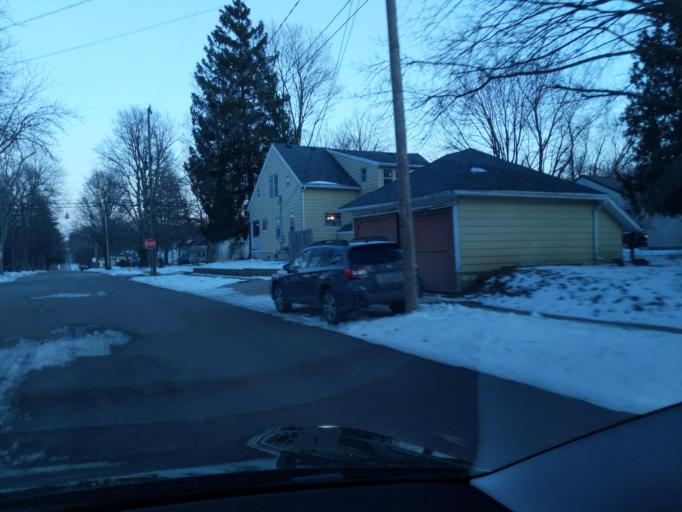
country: US
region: Michigan
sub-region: Ingham County
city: Mason
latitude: 42.5772
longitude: -84.4486
